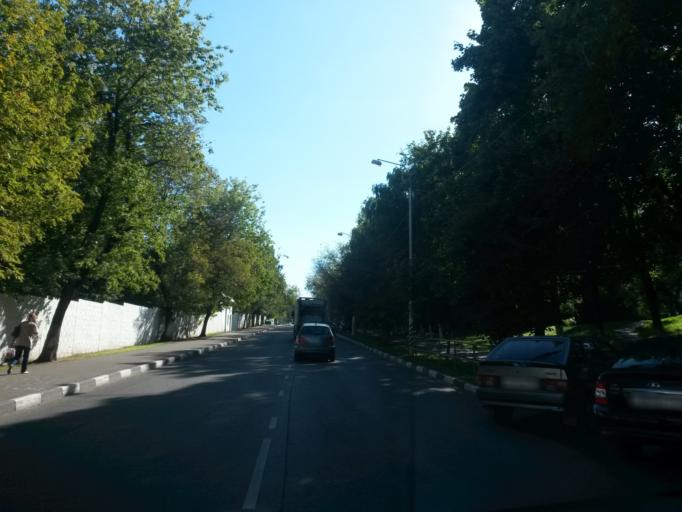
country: RU
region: Moscow
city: Zyuzino
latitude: 55.6548
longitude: 37.5828
